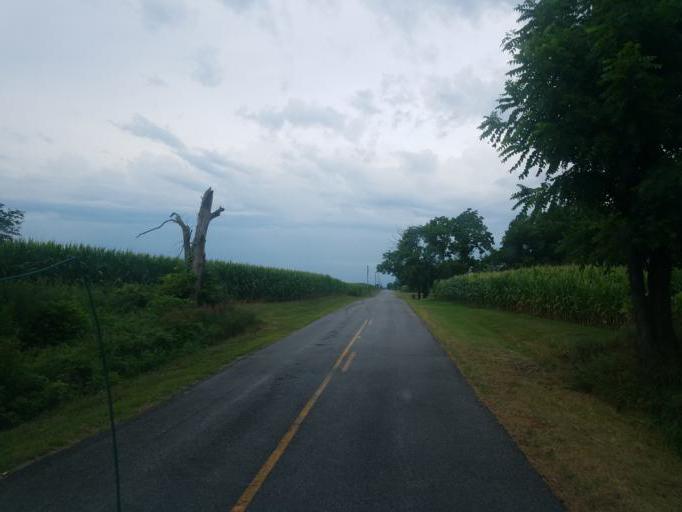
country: US
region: Ohio
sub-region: Paulding County
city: Antwerp
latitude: 41.2374
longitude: -84.7242
